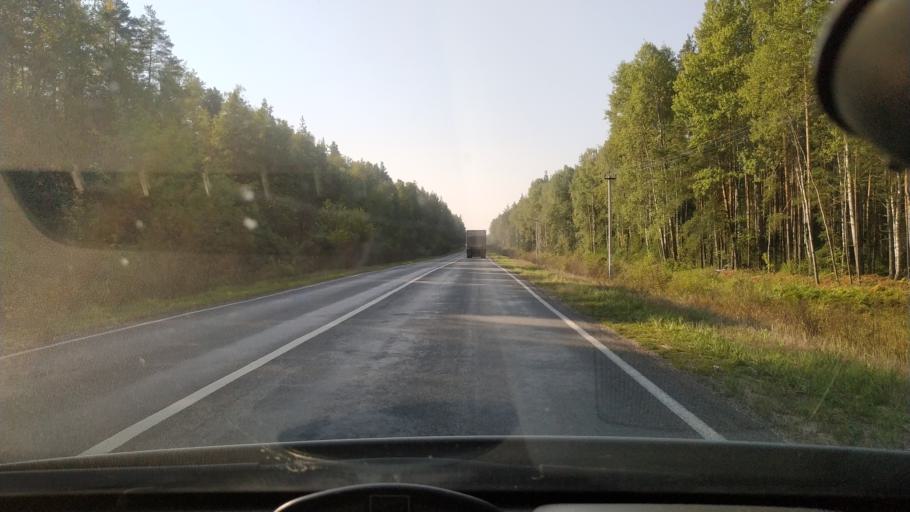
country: RU
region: Moskovskaya
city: Tugolesskiy Bor
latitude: 55.5010
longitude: 39.7136
